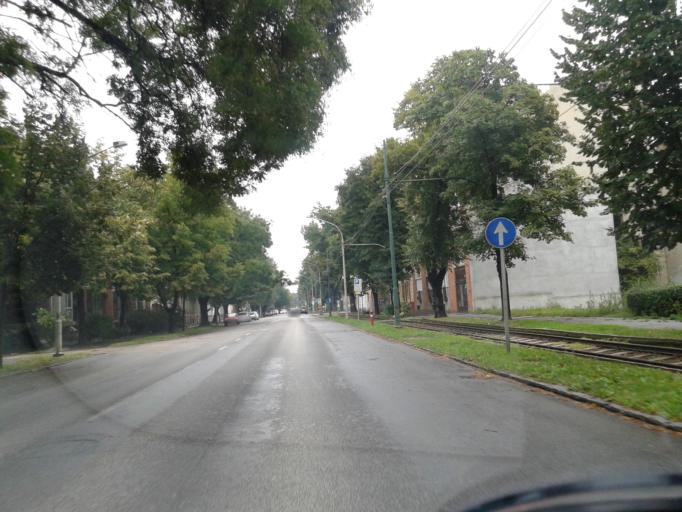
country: HU
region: Csongrad
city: Szeged
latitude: 46.2479
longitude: 20.1400
